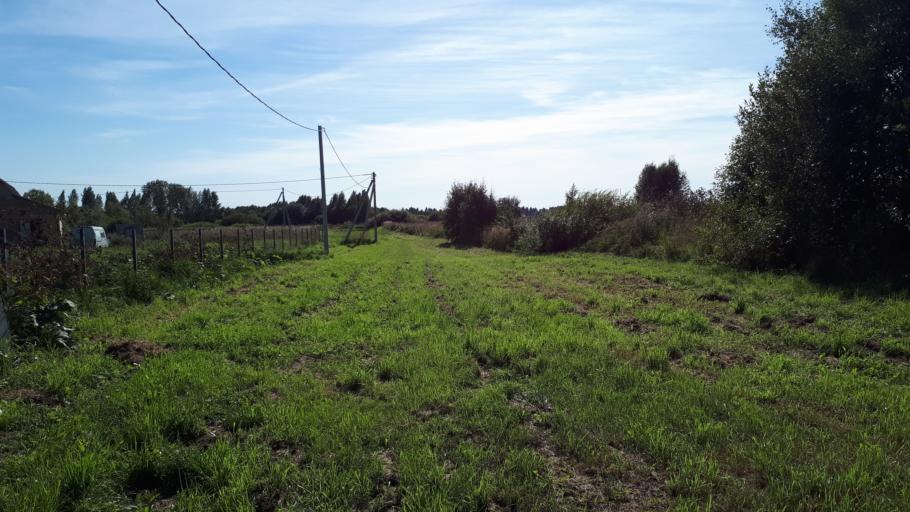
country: RU
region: Jaroslavl
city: Tunoshna
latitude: 57.6604
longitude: 40.0518
